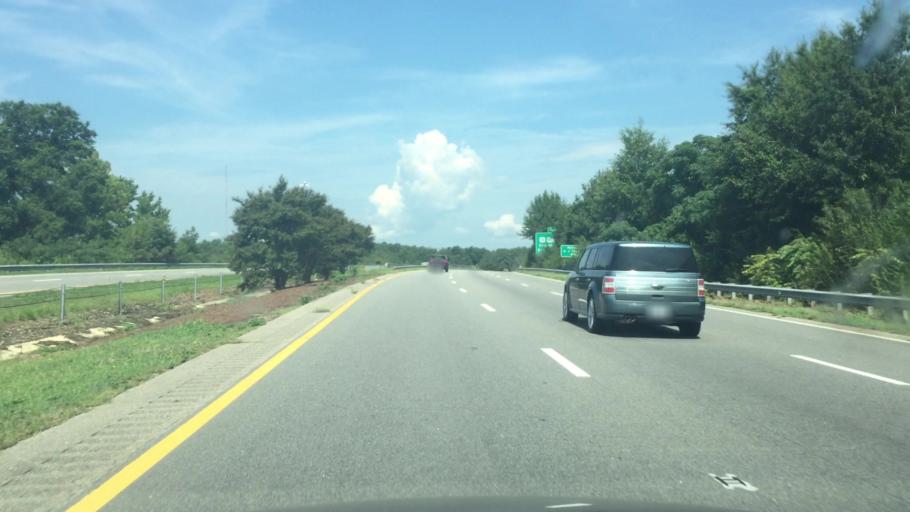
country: US
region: North Carolina
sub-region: Scotland County
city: Laurinburg
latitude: 34.7574
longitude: -79.4799
